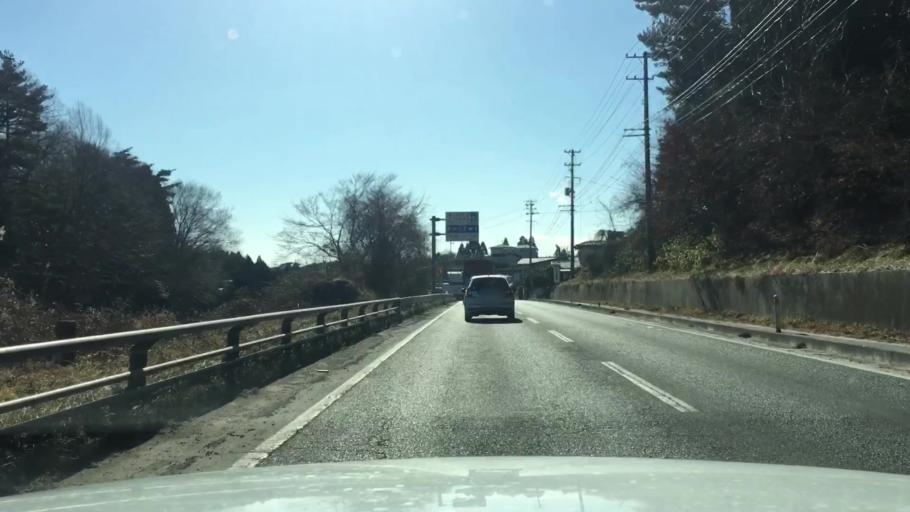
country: JP
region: Iwate
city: Yamada
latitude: 39.4411
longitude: 141.9719
